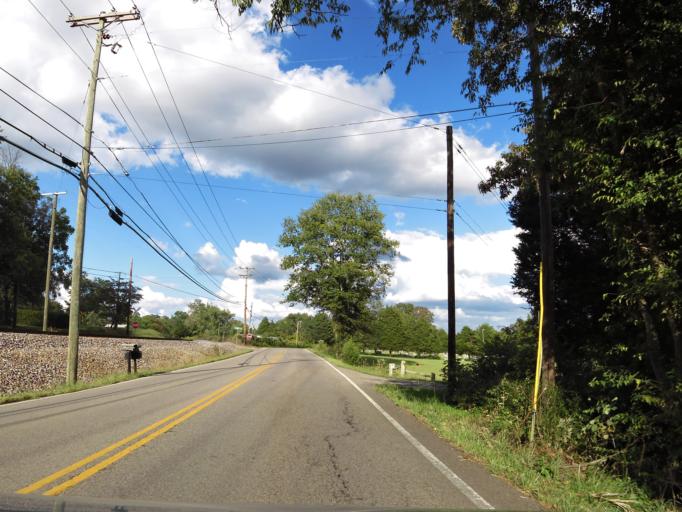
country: US
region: Tennessee
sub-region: Knox County
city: Mascot
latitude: 36.0686
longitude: -83.8461
